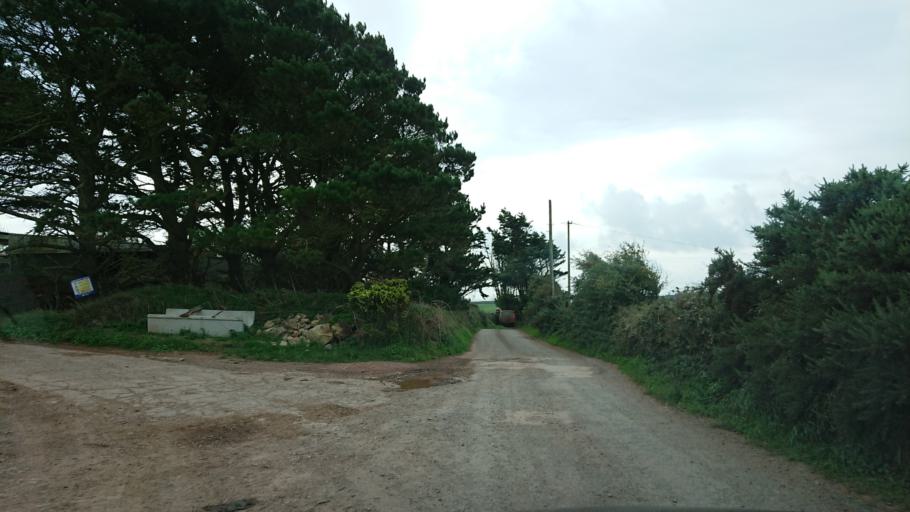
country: IE
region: Munster
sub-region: Waterford
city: Dunmore East
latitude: 52.1772
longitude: -6.9905
